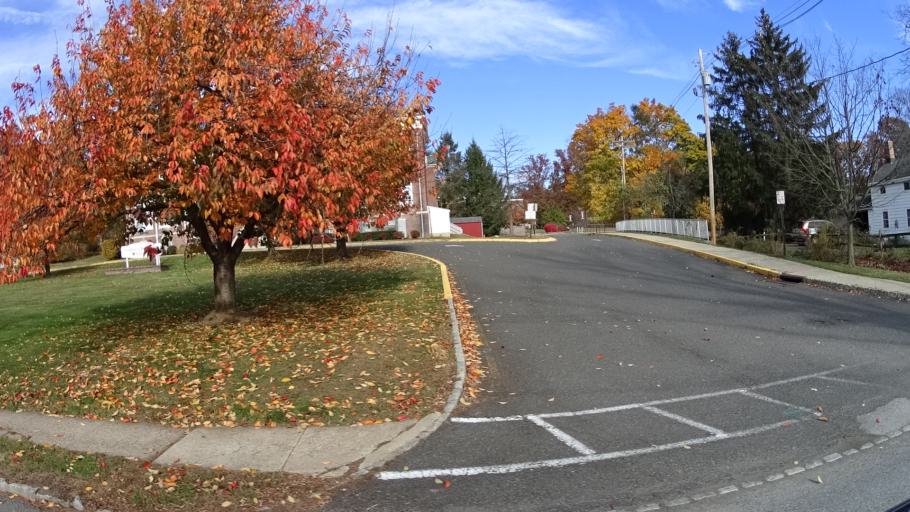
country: US
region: New Jersey
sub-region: Morris County
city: Madison
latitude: 40.7295
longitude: -74.4136
